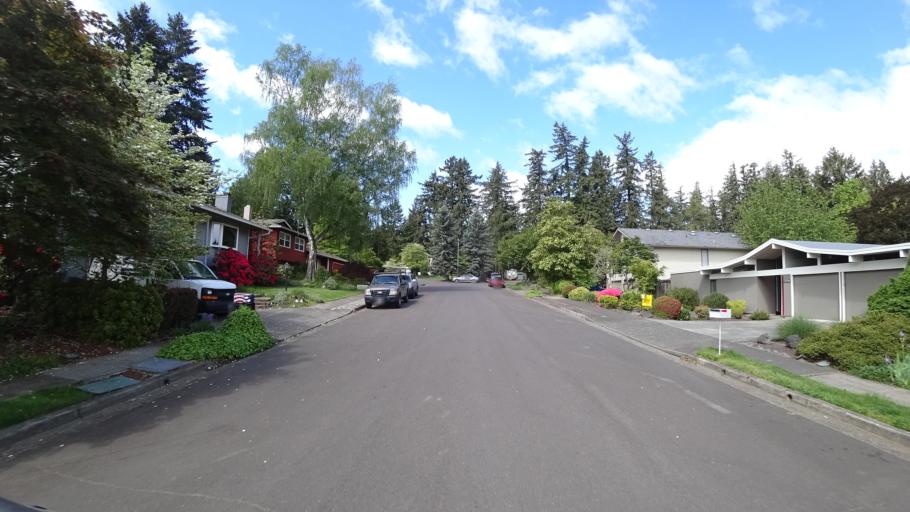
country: US
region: Oregon
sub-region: Washington County
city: Beaverton
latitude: 45.4674
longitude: -122.8117
